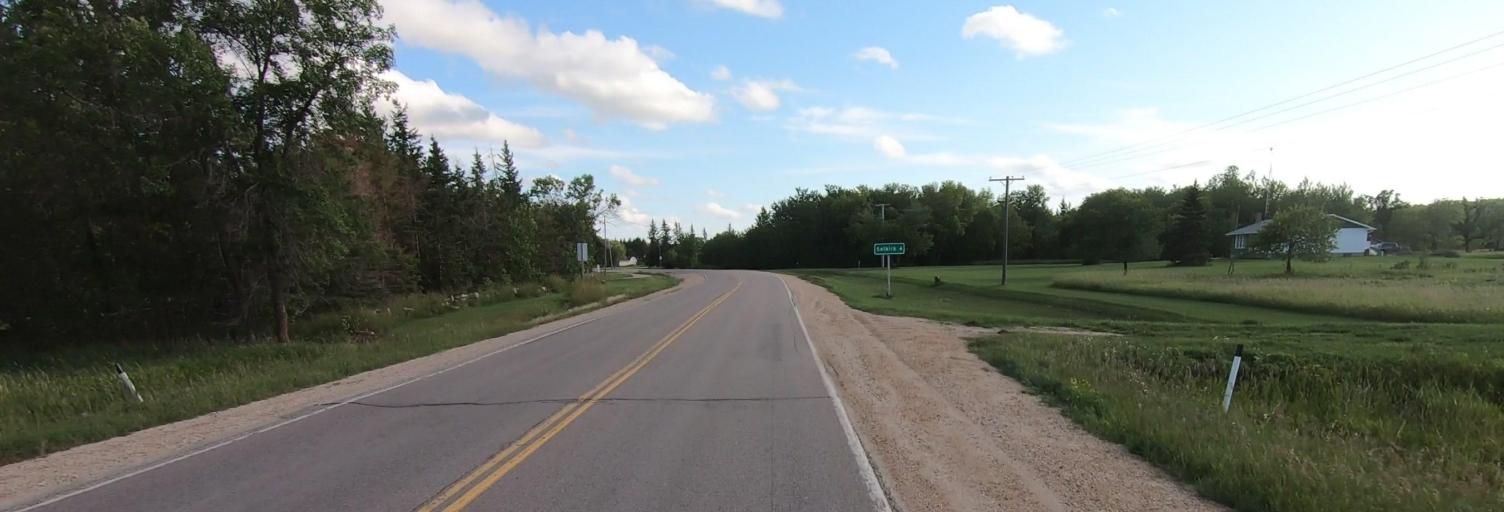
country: CA
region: Manitoba
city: Selkirk
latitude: 50.1883
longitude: -96.8456
